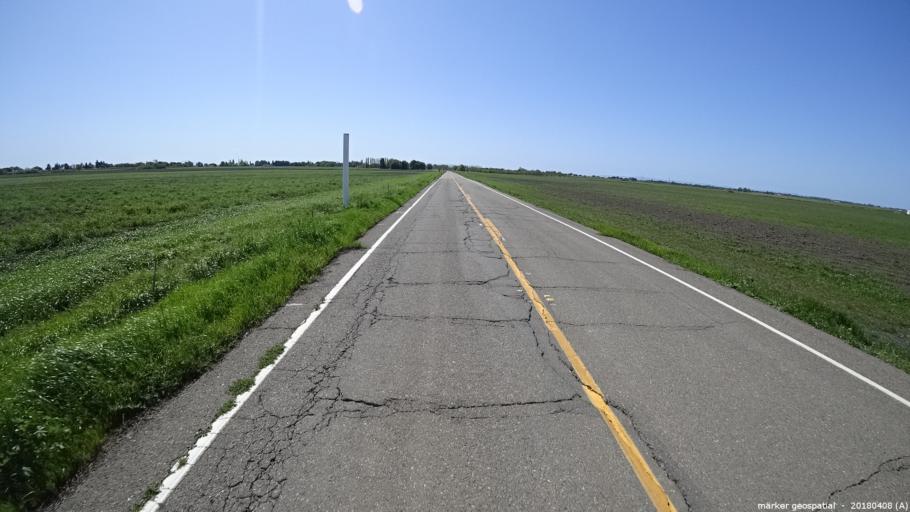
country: US
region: California
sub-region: Sacramento County
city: Walnut Grove
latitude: 38.2843
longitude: -121.5261
